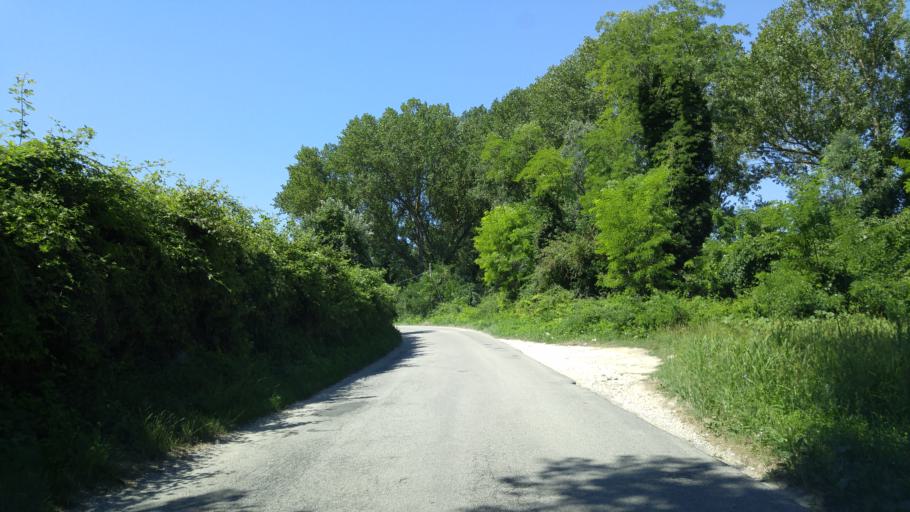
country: IT
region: The Marches
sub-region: Provincia di Pesaro e Urbino
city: Fenile
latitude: 43.8357
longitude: 12.9625
